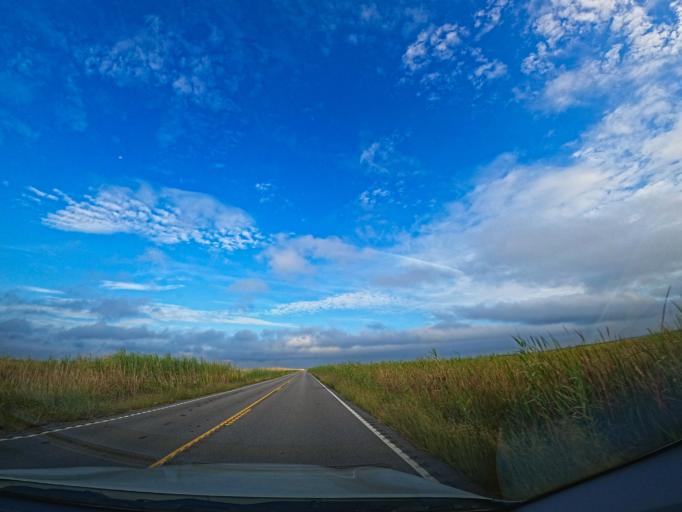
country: US
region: Louisiana
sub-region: Terrebonne Parish
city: Dulac
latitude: 29.3253
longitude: -90.6838
